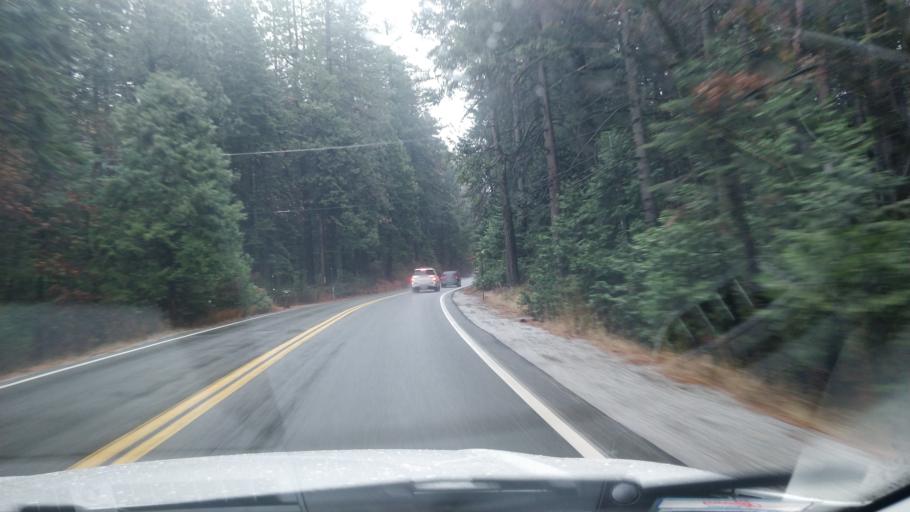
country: US
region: California
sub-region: Nevada County
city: Nevada City
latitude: 39.3229
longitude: -120.8532
